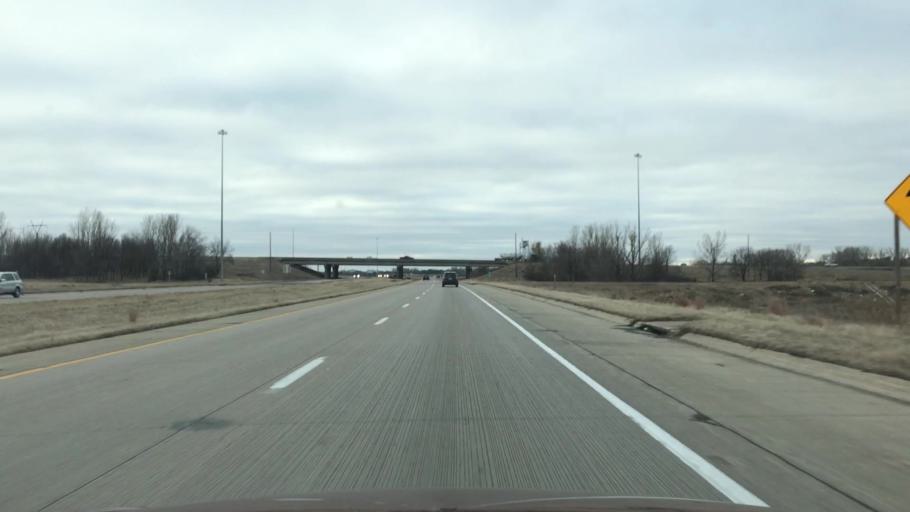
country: US
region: Iowa
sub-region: Woodbury County
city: Sioux City
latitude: 42.4787
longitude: -96.3241
